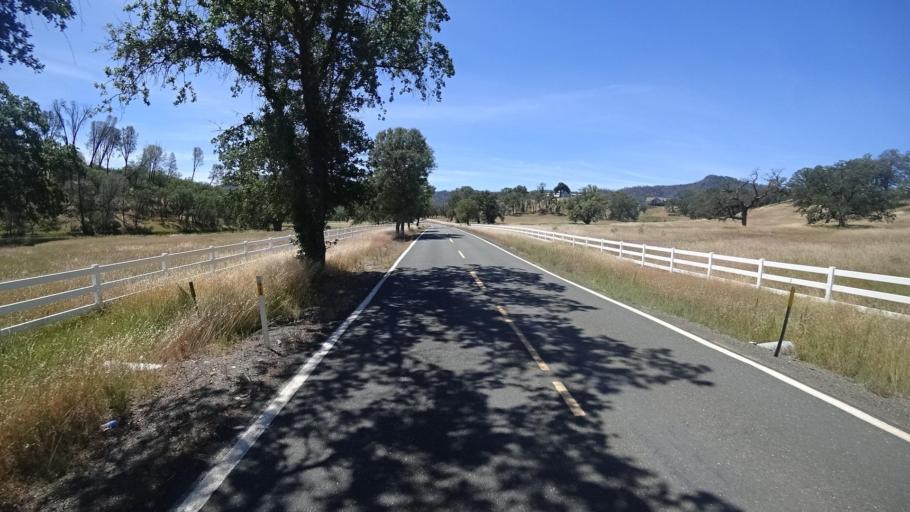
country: US
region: California
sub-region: Lake County
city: Middletown
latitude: 38.7278
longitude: -122.5414
